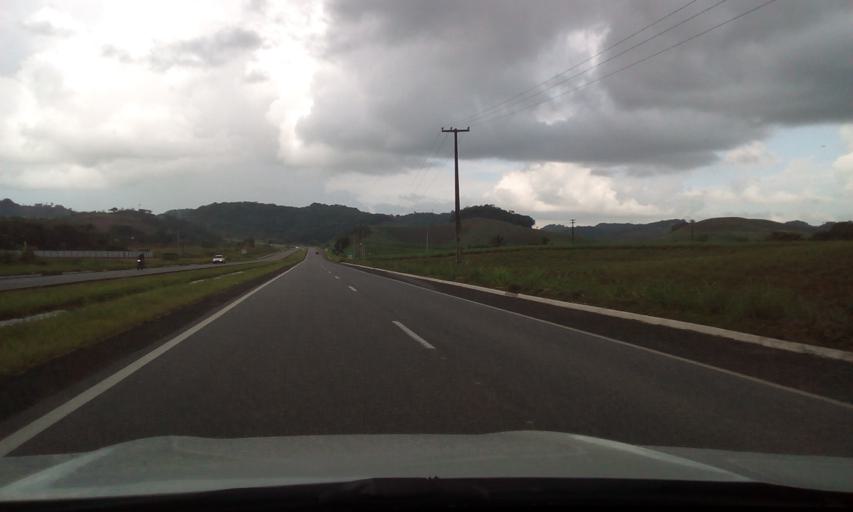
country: BR
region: Pernambuco
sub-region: Cabo De Santo Agostinho
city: Cabo
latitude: -8.2556
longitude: -35.0358
